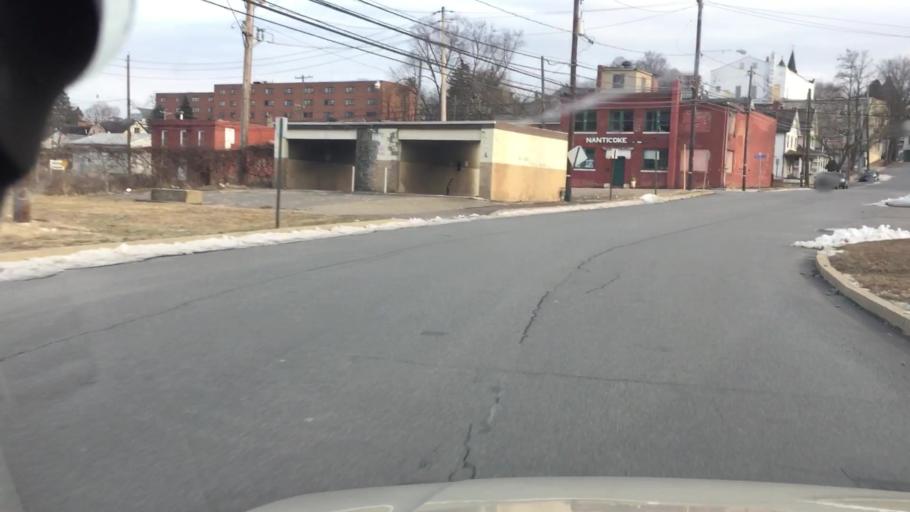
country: US
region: Pennsylvania
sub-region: Luzerne County
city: Nanticoke
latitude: 41.2071
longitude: -76.0027
